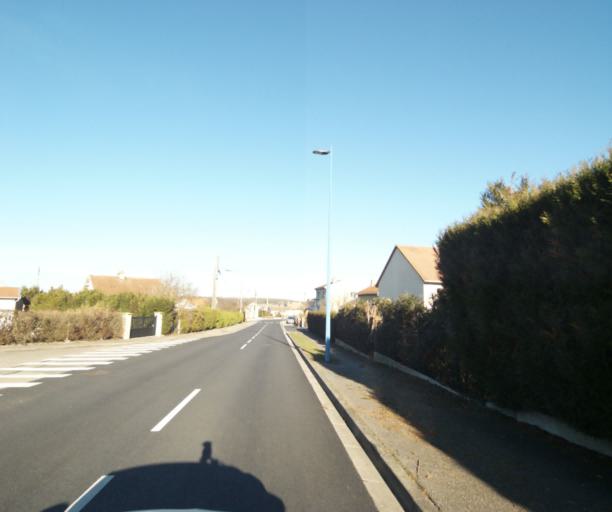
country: FR
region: Lorraine
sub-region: Departement de Meurthe-et-Moselle
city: Heillecourt
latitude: 48.6593
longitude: 6.2173
